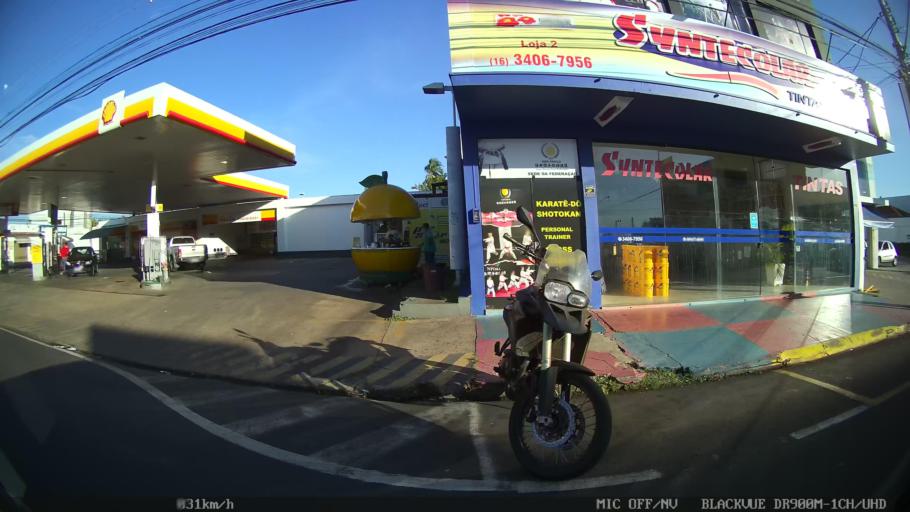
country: BR
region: Sao Paulo
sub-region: Franca
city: Franca
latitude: -20.5267
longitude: -47.3800
